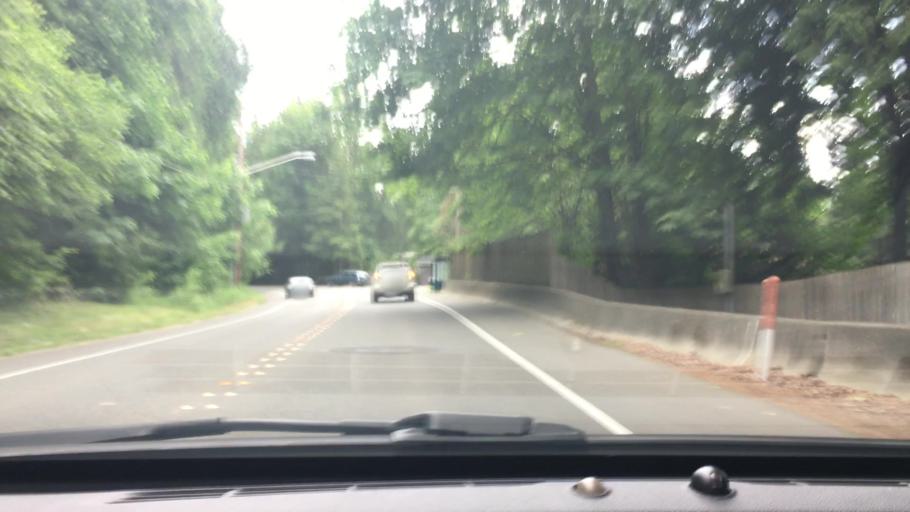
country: US
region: Washington
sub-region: King County
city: West Lake Sammamish
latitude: 47.5615
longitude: -122.0889
